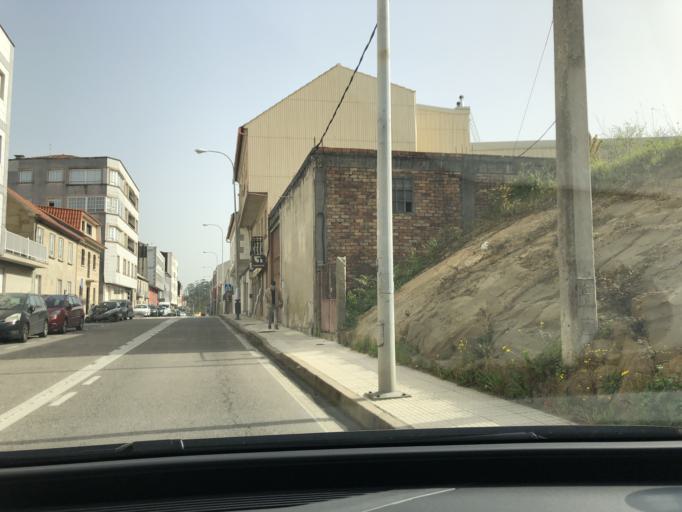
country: ES
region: Galicia
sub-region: Provincia de Pontevedra
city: Marin
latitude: 42.3714
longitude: -8.7299
